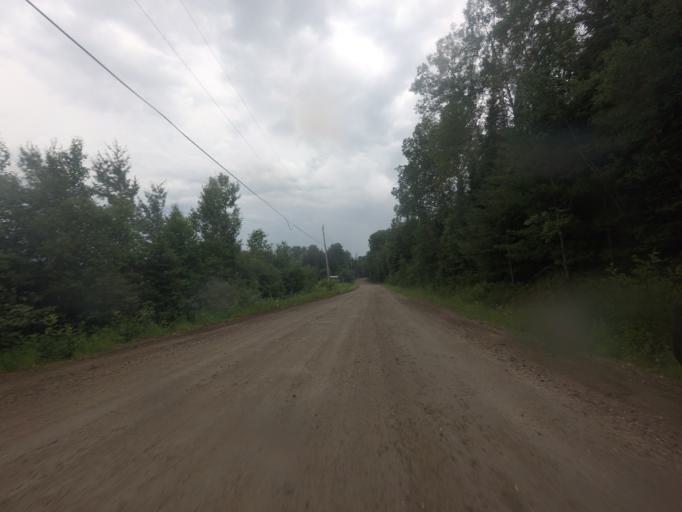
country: CA
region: Quebec
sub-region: Outaouais
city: Maniwaki
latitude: 46.4449
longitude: -75.9347
